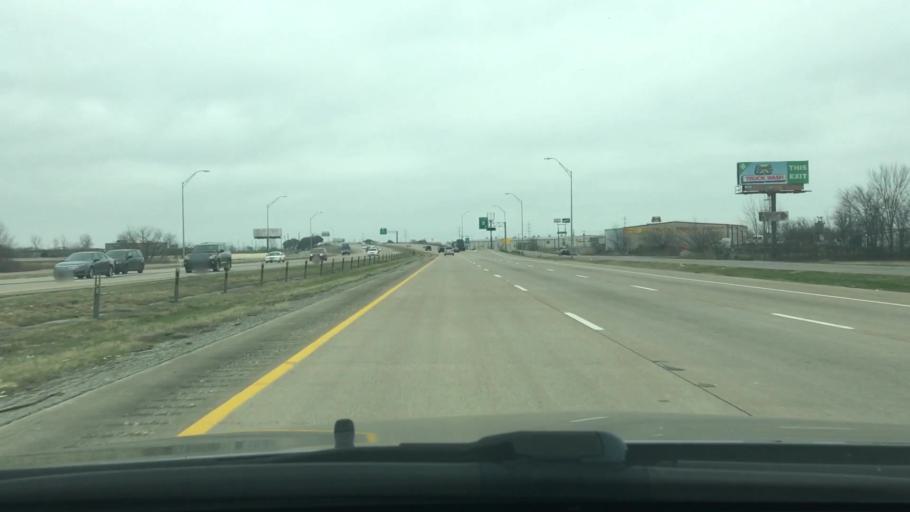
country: US
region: Texas
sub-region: Ellis County
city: Ennis
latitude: 32.3151
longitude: -96.6014
